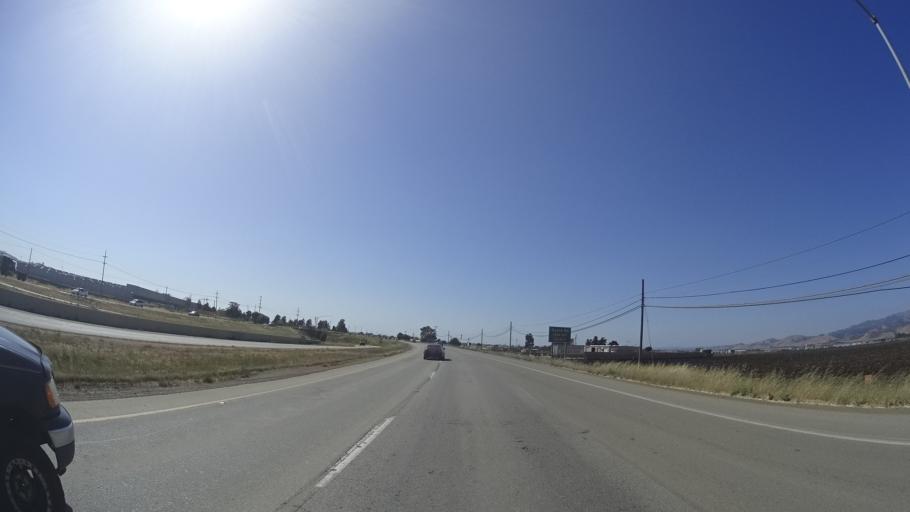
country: US
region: California
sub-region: Monterey County
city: Chualar
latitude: 36.6256
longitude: -121.5838
